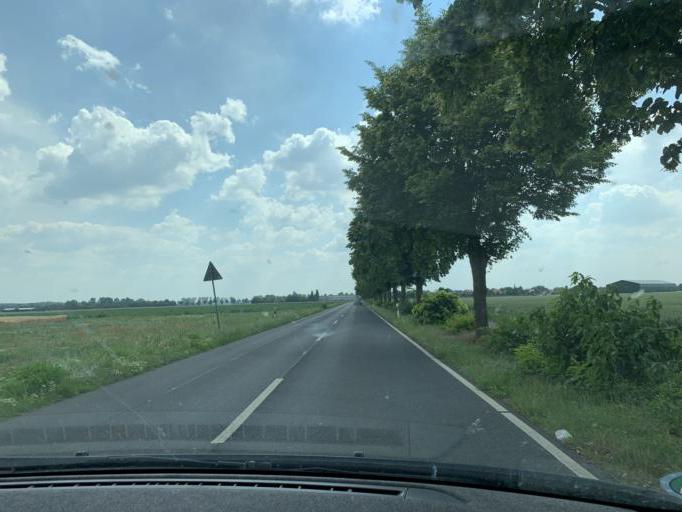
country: DE
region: North Rhine-Westphalia
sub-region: Regierungsbezirk Koln
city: Elsdorf
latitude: 50.9339
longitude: 6.6006
